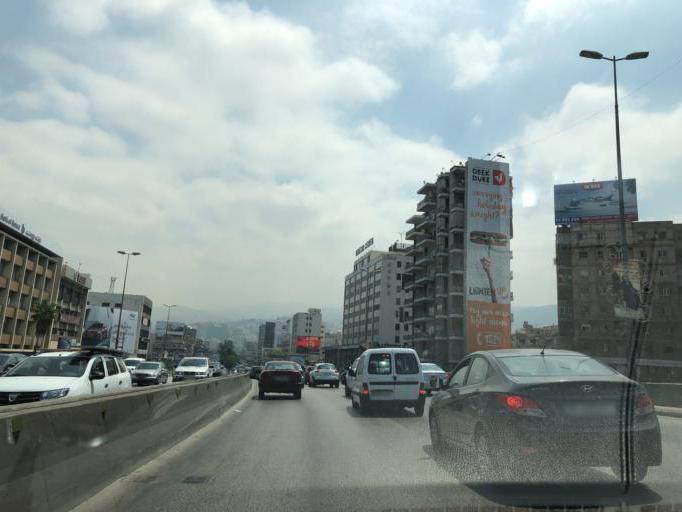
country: LB
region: Mont-Liban
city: Jdaidet el Matn
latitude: 33.8937
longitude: 35.5510
